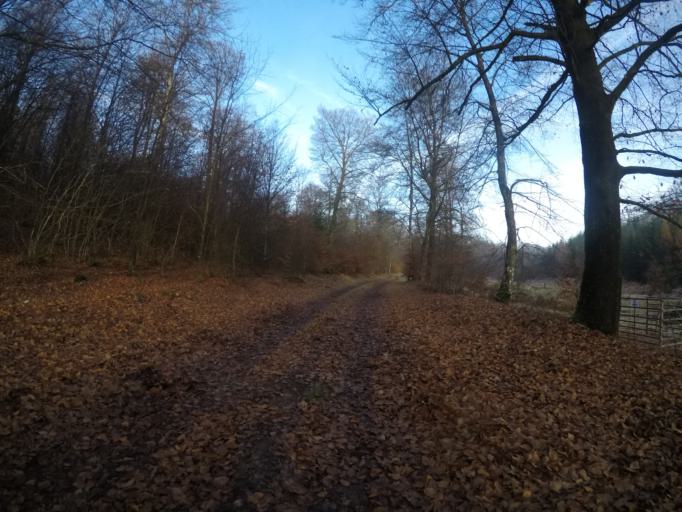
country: BE
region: Wallonia
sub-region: Province du Luxembourg
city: Habay-la-Vieille
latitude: 49.7647
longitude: 5.6587
